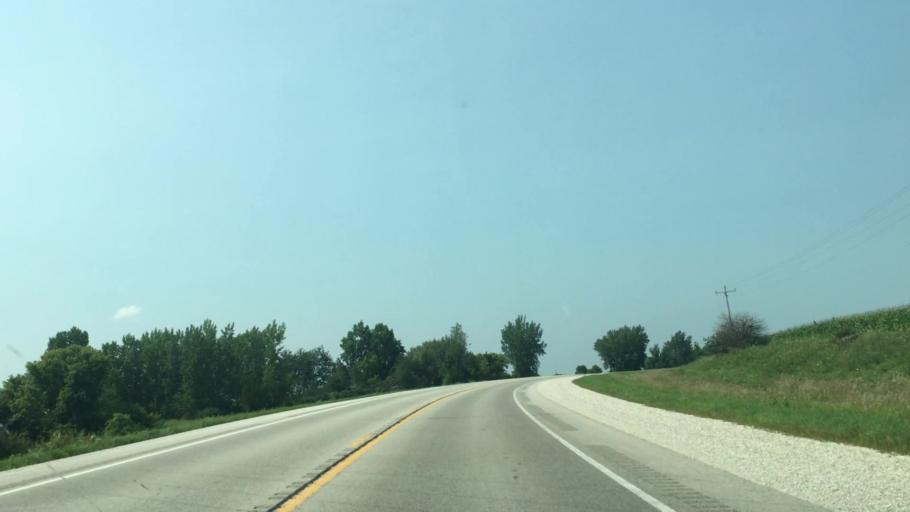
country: US
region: Iowa
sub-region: Winneshiek County
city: Decorah
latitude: 43.1943
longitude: -91.8721
